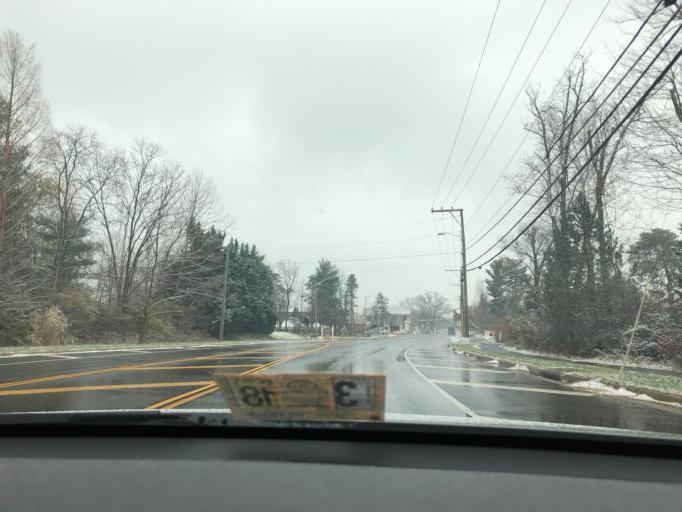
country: US
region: Virginia
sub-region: Fairfax County
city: Oakton
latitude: 38.8861
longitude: -77.3015
